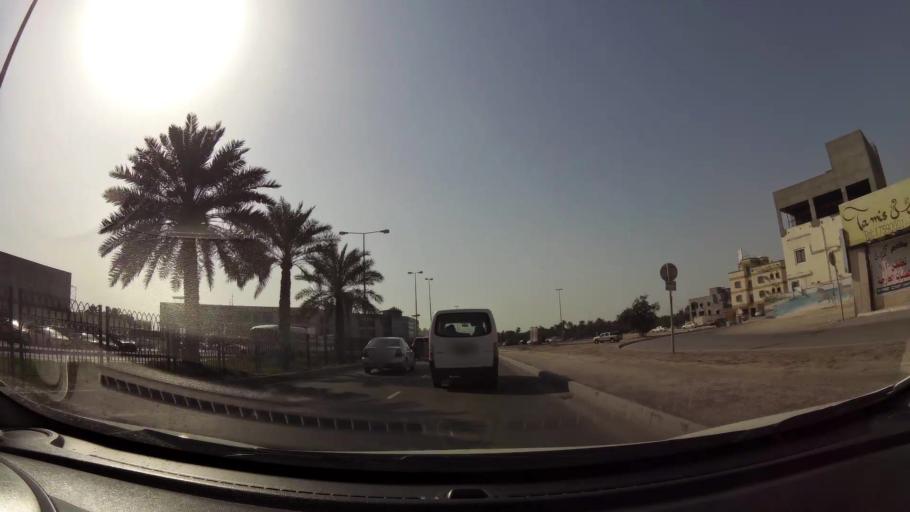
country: BH
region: Manama
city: Jidd Hafs
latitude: 26.2194
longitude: 50.5123
